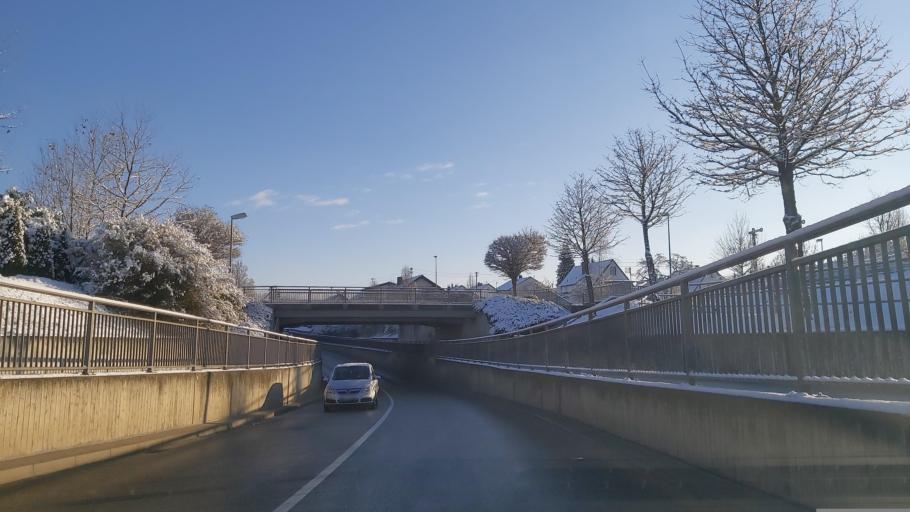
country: DE
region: Bavaria
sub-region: Swabia
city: Vohringen
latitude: 48.2770
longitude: 10.0832
